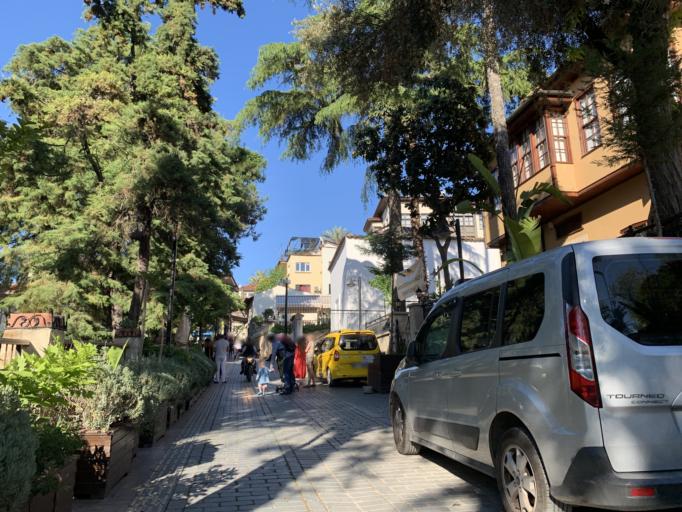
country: TR
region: Antalya
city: Antalya
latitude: 36.8835
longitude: 30.7037
